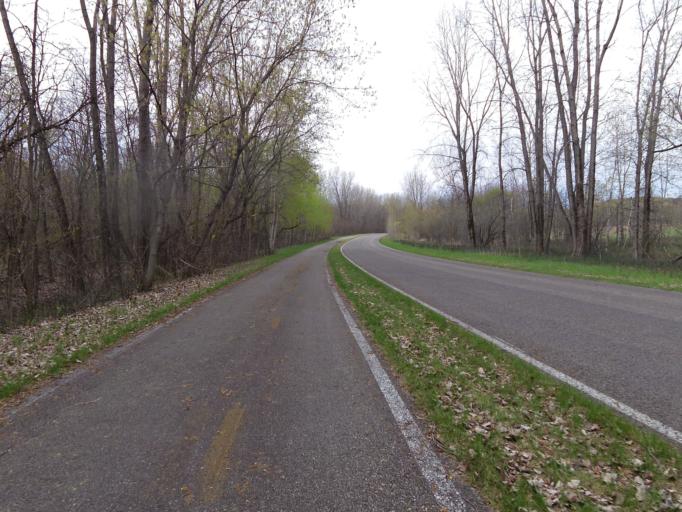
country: CA
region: Quebec
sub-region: Laurentides
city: Oka
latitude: 45.4855
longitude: -74.0215
